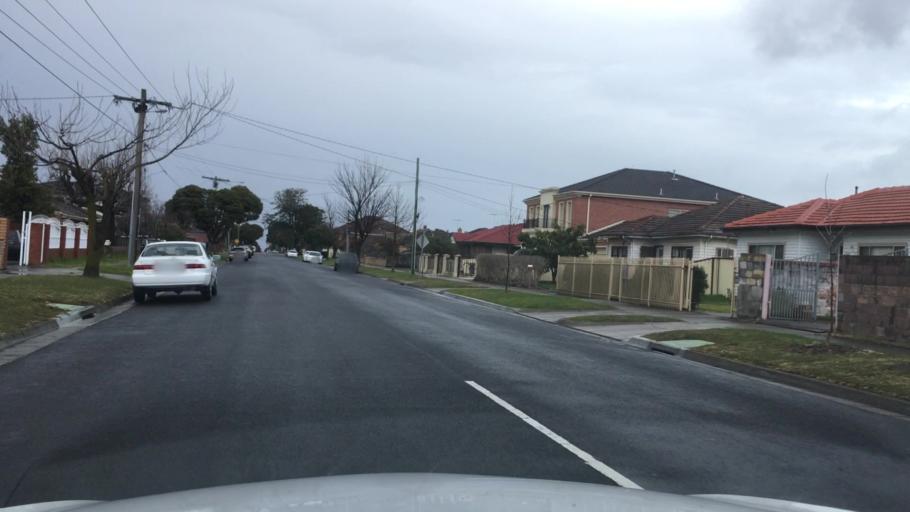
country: AU
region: Victoria
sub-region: Greater Dandenong
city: Springvale
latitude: -37.9468
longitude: 145.1456
